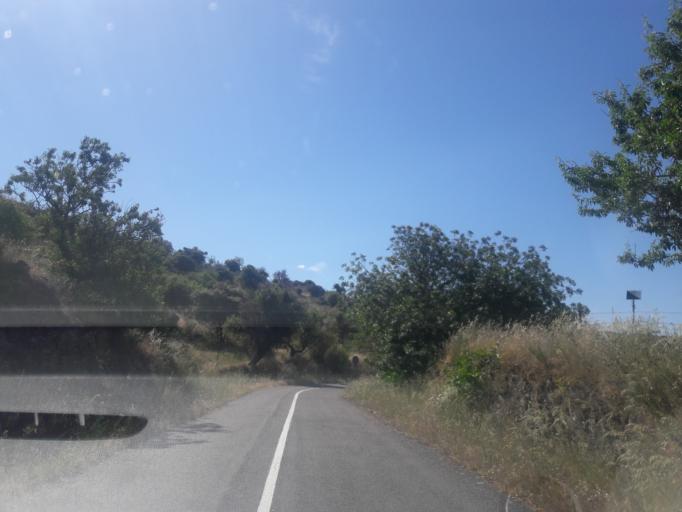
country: ES
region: Castille and Leon
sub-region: Provincia de Salamanca
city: Saucelle
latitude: 41.0192
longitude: -6.7505
